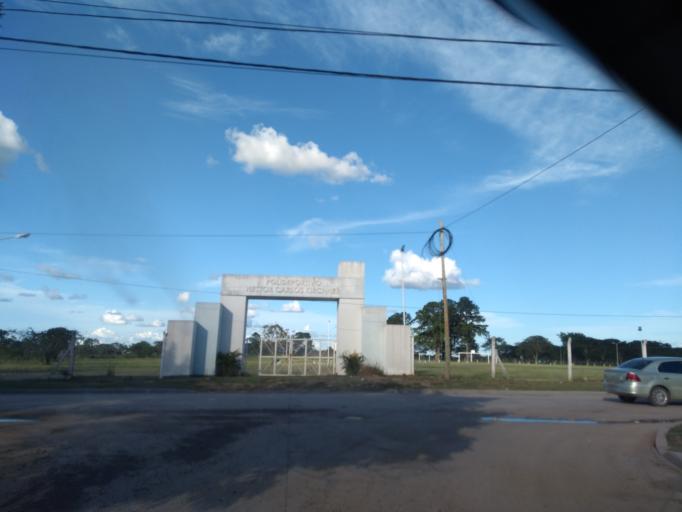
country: AR
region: Chaco
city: Fontana
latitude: -27.4113
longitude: -59.0390
